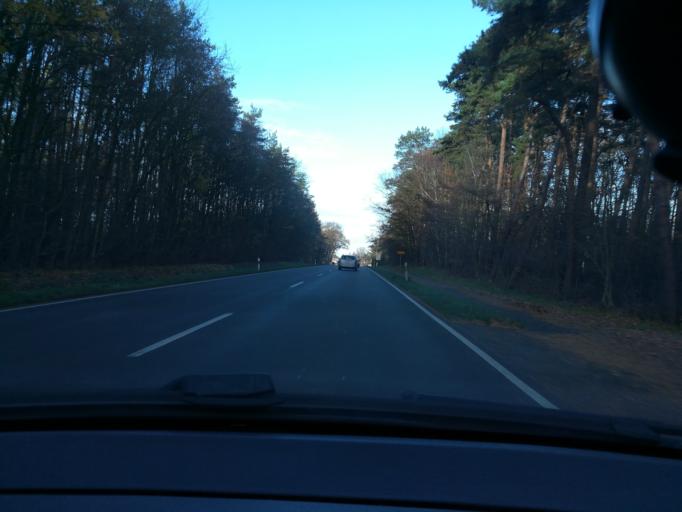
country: DE
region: Lower Saxony
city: Kirchdorf
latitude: 52.5861
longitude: 8.8386
